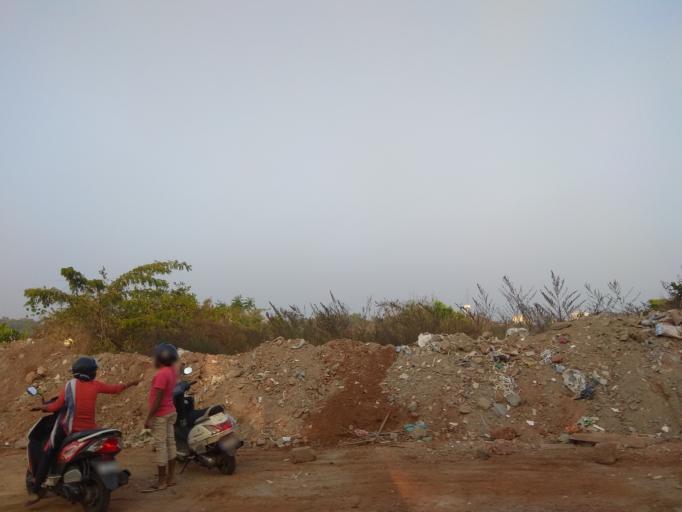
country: IN
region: Karnataka
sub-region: Dakshina Kannada
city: Mangalore
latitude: 12.9170
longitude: 74.8592
